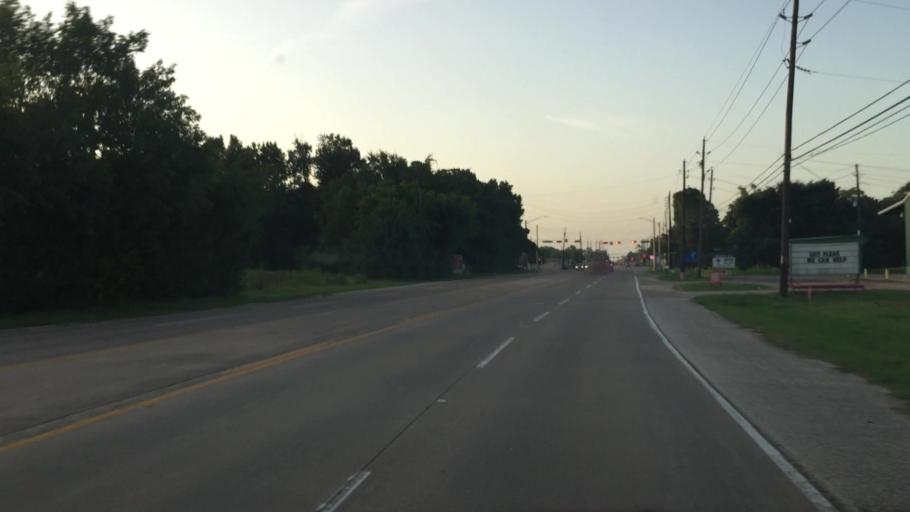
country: US
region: Texas
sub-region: Harris County
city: Hudson
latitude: 29.9935
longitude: -95.5026
